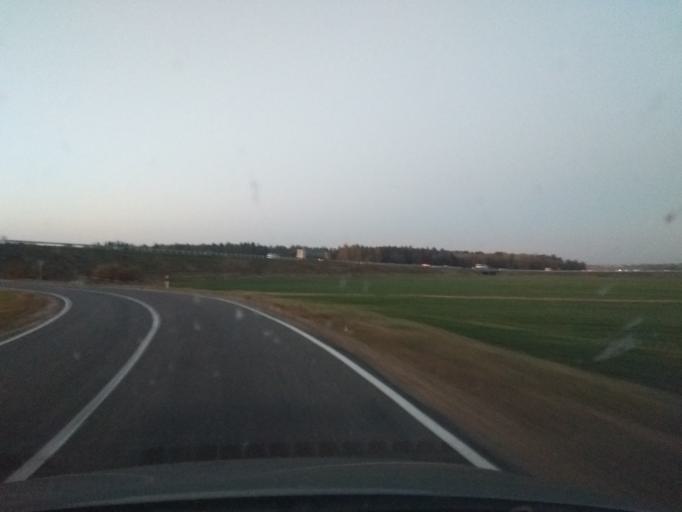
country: BY
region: Minsk
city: Dzyarzhynsk
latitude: 53.6540
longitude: 27.0813
